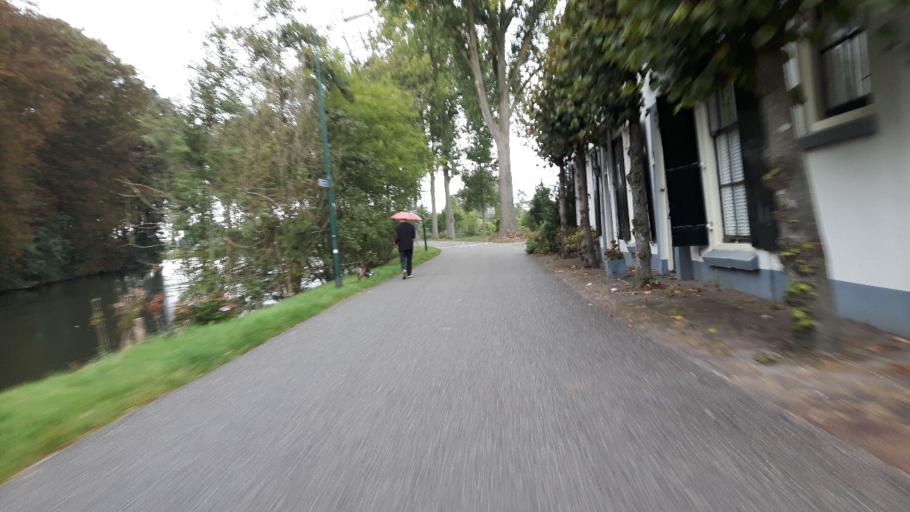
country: NL
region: Utrecht
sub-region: Stichtse Vecht
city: Maarssen
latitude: 52.1297
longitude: 5.0691
